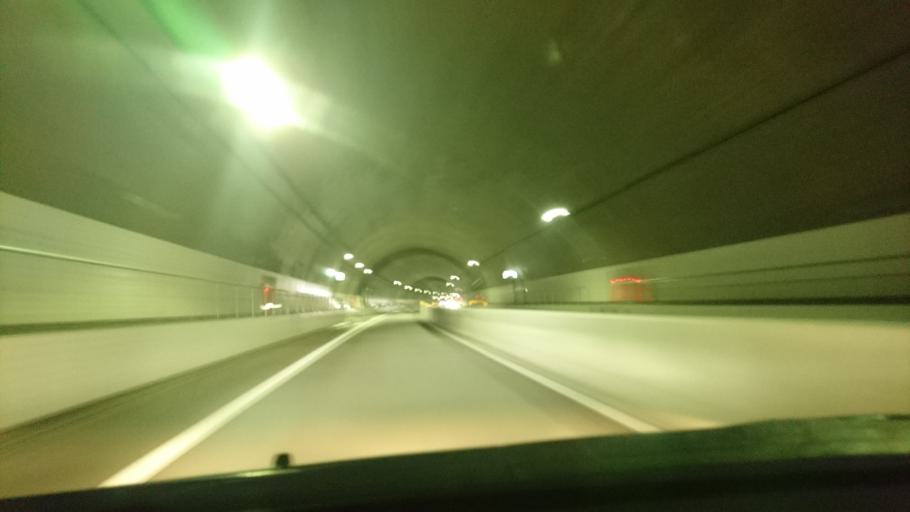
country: JP
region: Iwate
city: Miyako
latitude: 39.8082
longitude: 141.9563
